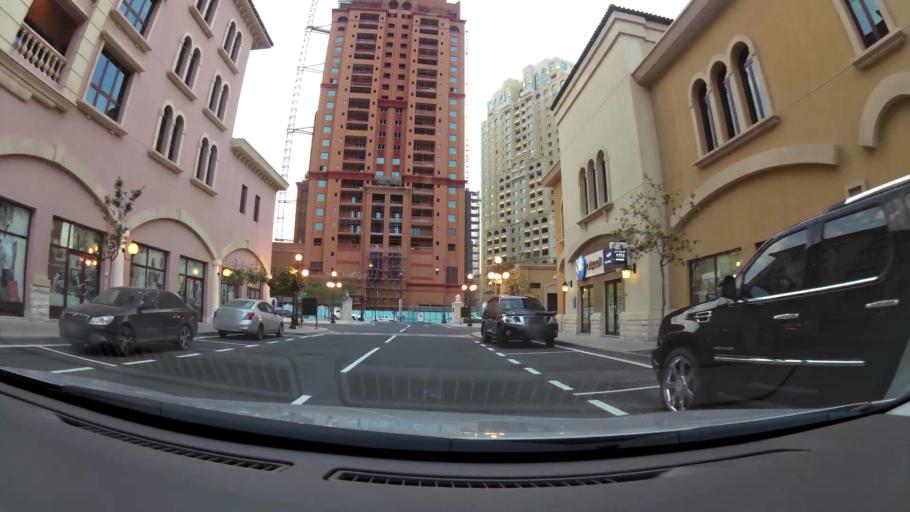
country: QA
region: Baladiyat ad Dawhah
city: Doha
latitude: 25.3696
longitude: 51.5505
